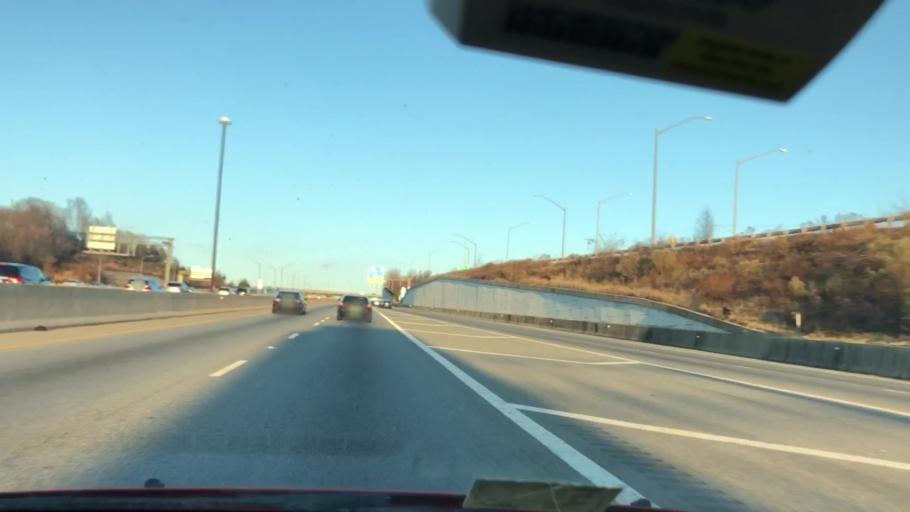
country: US
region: Maryland
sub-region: Prince George's County
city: Forest Heights
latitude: 38.7970
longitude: -77.0086
